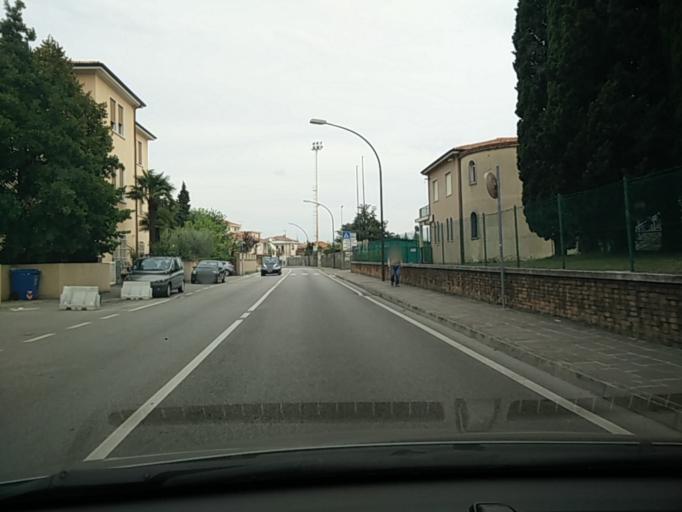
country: IT
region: Veneto
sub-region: Provincia di Treviso
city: Treviso
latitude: 45.6596
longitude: 12.2548
